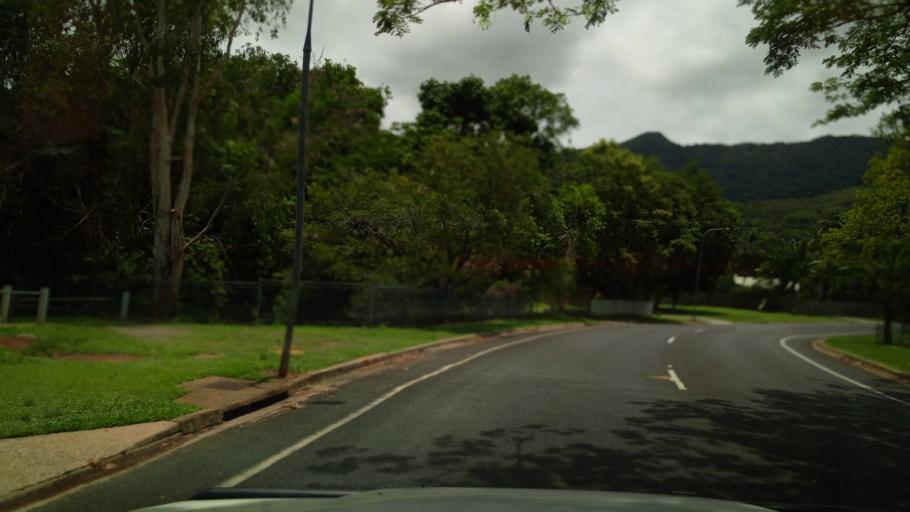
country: AU
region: Queensland
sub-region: Cairns
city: Yorkeys Knob
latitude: -16.8331
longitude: 145.6908
